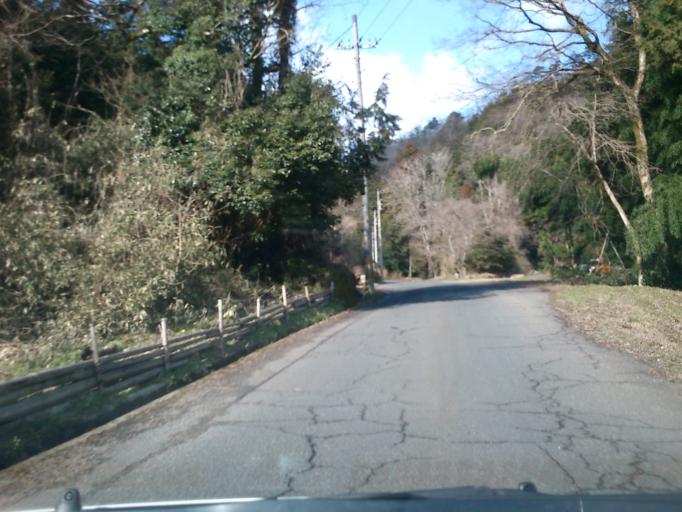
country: JP
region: Kyoto
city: Miyazu
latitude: 35.5820
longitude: 135.1772
